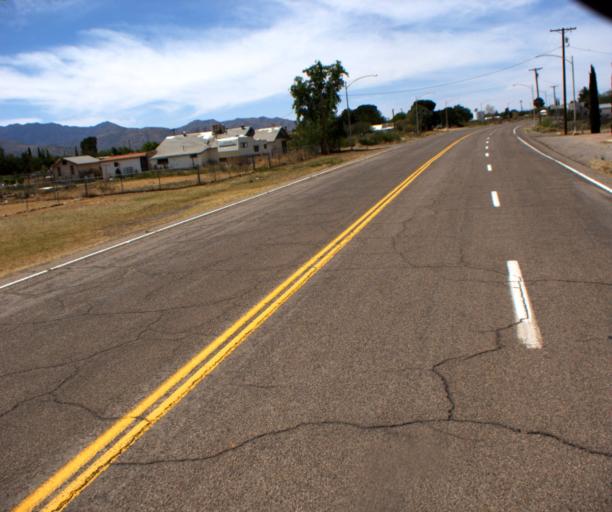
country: US
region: Arizona
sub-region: Cochise County
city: Willcox
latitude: 32.3253
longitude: -109.4809
